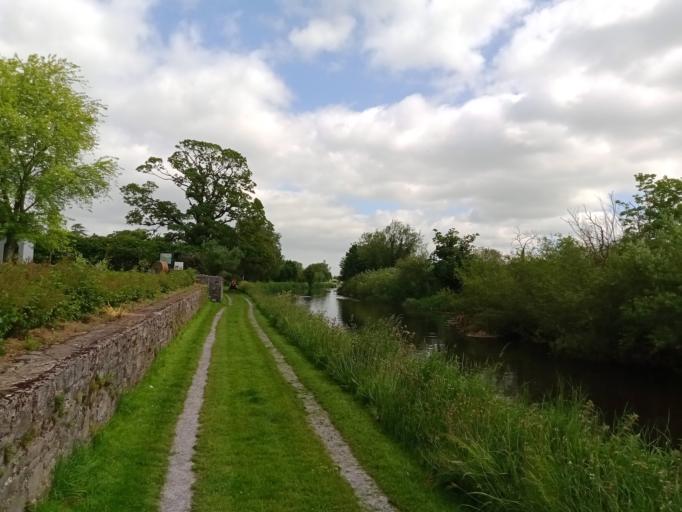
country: IE
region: Leinster
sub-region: County Carlow
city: Bagenalstown
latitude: 52.7369
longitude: -6.9786
